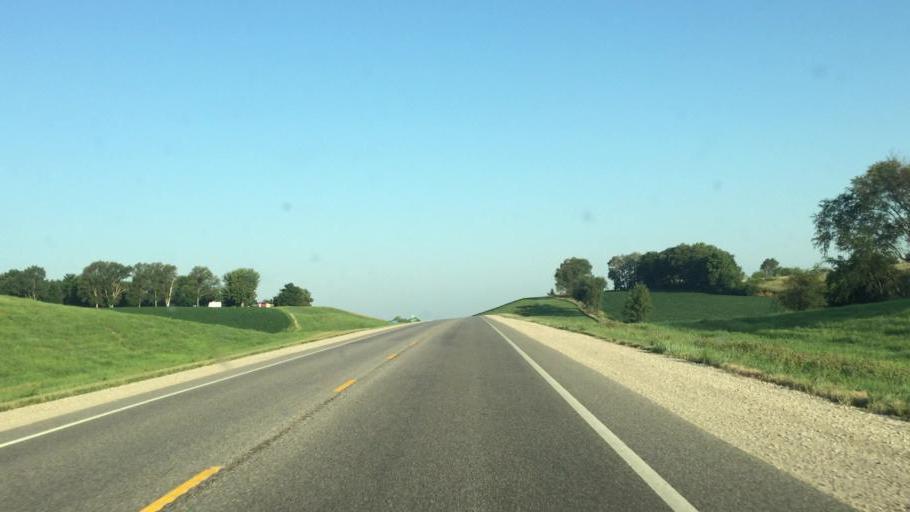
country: US
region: Kansas
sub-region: Doniphan County
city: Troy
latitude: 39.7935
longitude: -95.0785
